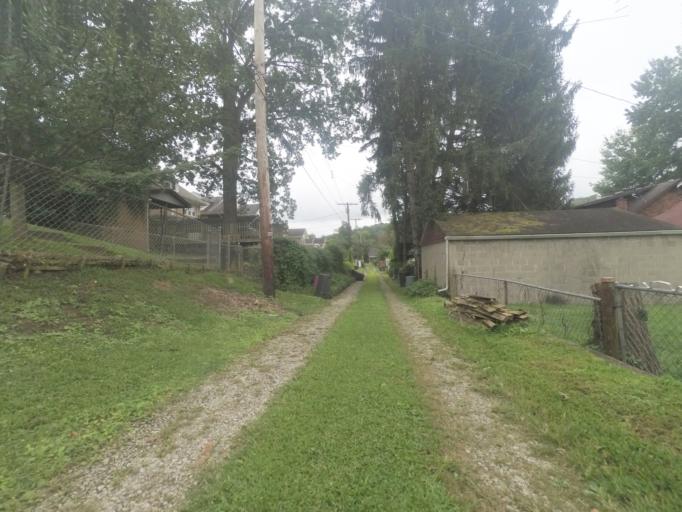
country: US
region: West Virginia
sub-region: Cabell County
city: Huntington
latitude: 38.4075
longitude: -82.4296
